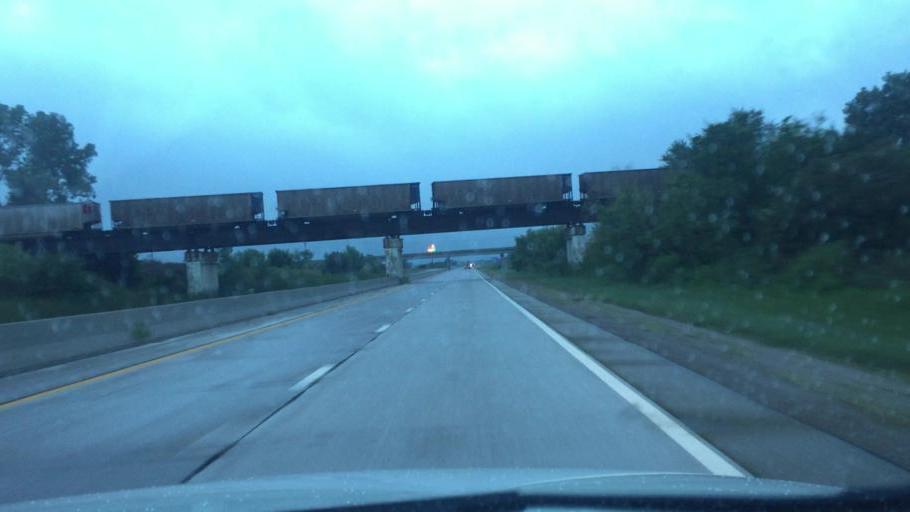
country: US
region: Kansas
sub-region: Neosho County
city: Chanute
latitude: 37.6631
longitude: -95.4796
